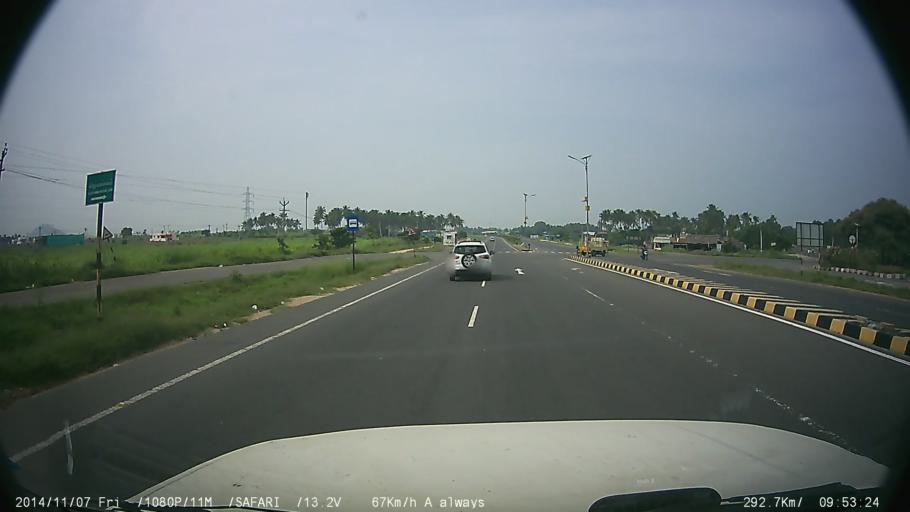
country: IN
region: Tamil Nadu
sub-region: Erode
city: Vijayapuri
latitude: 11.2438
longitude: 77.5161
